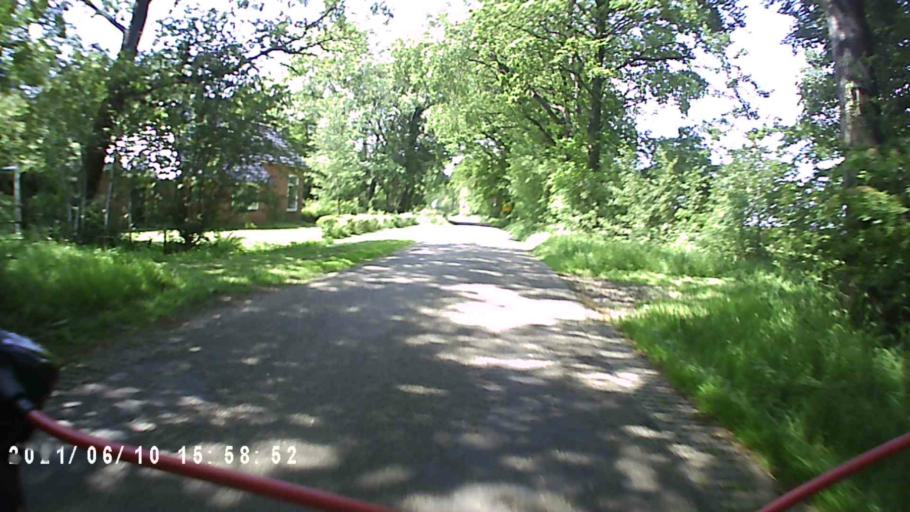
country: NL
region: Friesland
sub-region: Gemeente Achtkarspelen
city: Kootstertille
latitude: 53.1929
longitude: 6.0887
